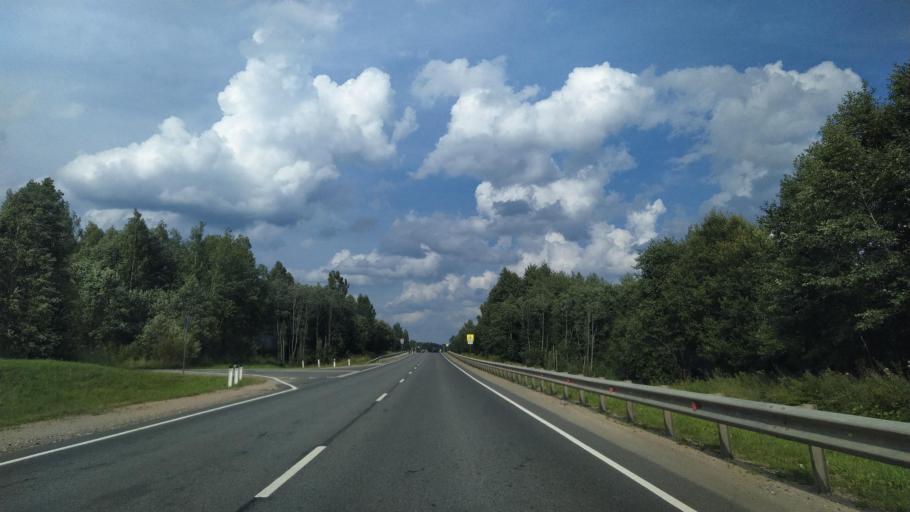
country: RU
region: Novgorod
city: Sol'tsy
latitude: 58.1549
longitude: 30.4408
